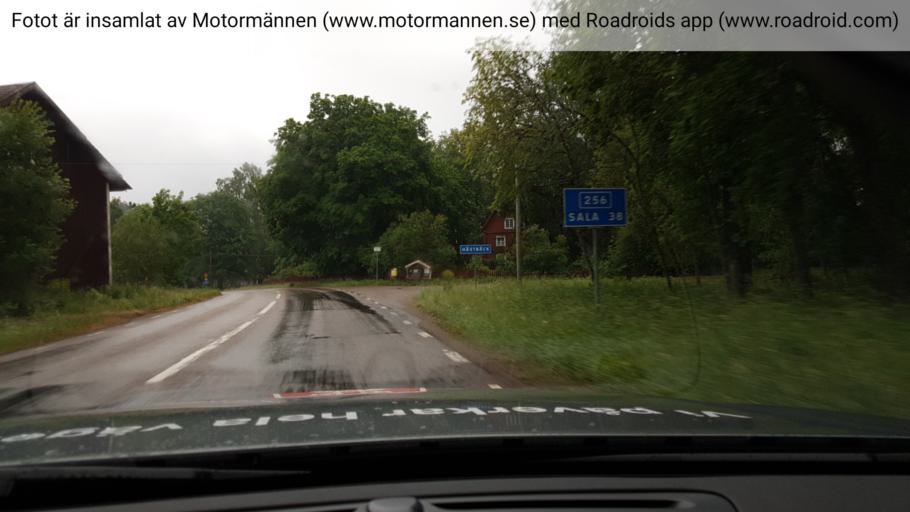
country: SE
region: Dalarna
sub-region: Avesta Kommun
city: Avesta
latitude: 59.9984
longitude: 16.0821
